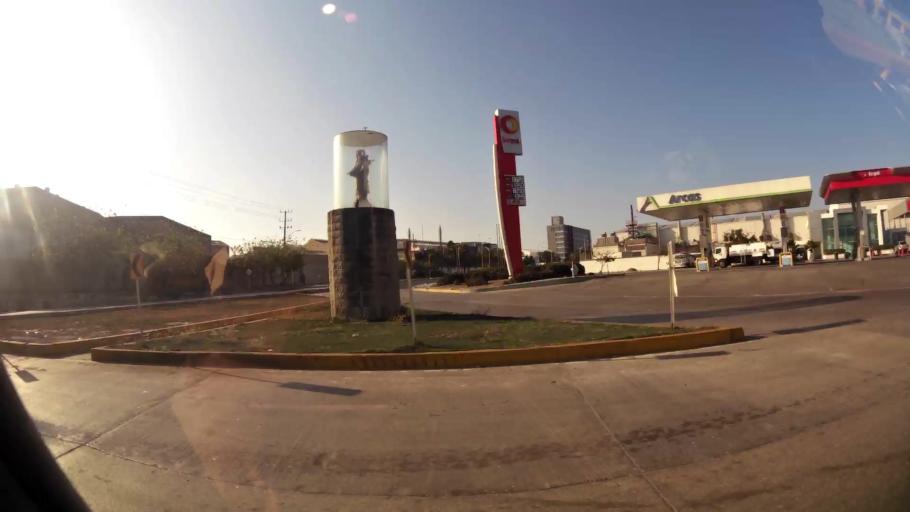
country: CO
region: Atlantico
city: Barranquilla
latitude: 11.0385
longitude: -74.8270
